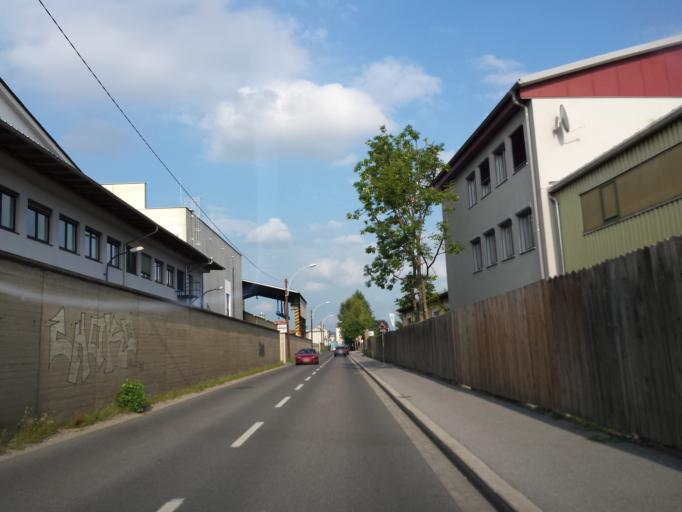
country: AT
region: Styria
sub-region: Graz Stadt
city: Wetzelsdorf
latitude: 47.0686
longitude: 15.4123
